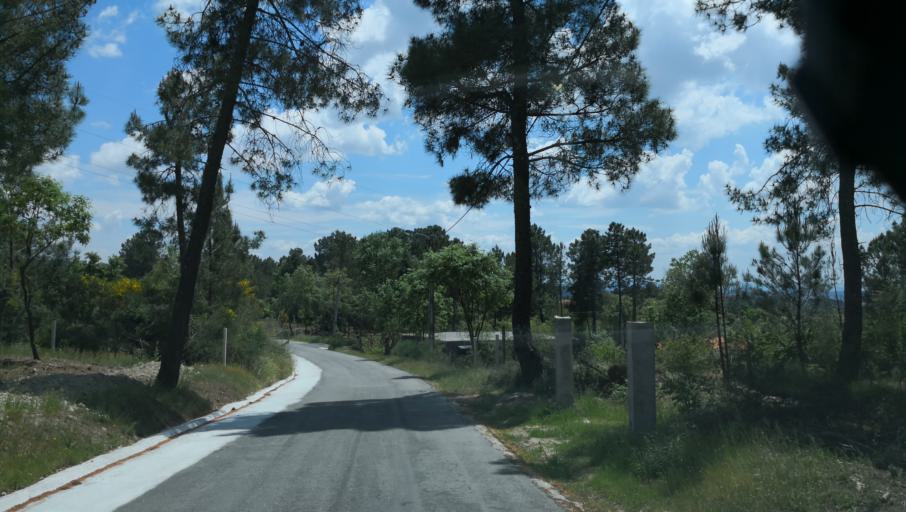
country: PT
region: Vila Real
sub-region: Vila Real
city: Vila Real
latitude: 41.3523
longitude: -7.7257
